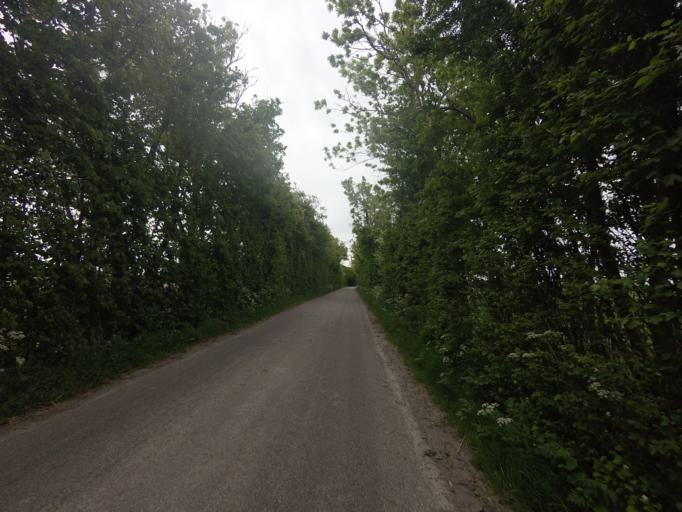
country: NL
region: Zeeland
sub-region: Gemeente Middelburg
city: Middelburg
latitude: 51.5528
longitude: 3.5437
